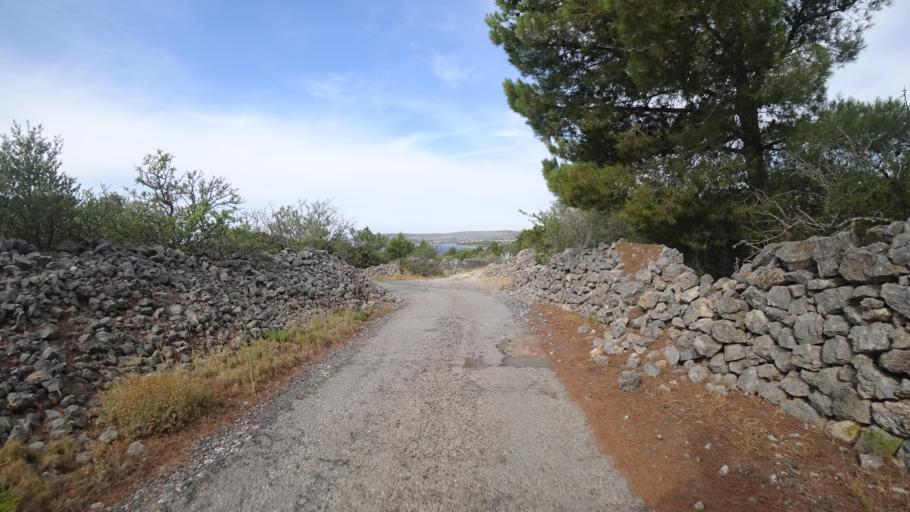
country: FR
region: Languedoc-Roussillon
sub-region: Departement de l'Aude
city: Leucate
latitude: 42.9045
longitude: 3.0235
